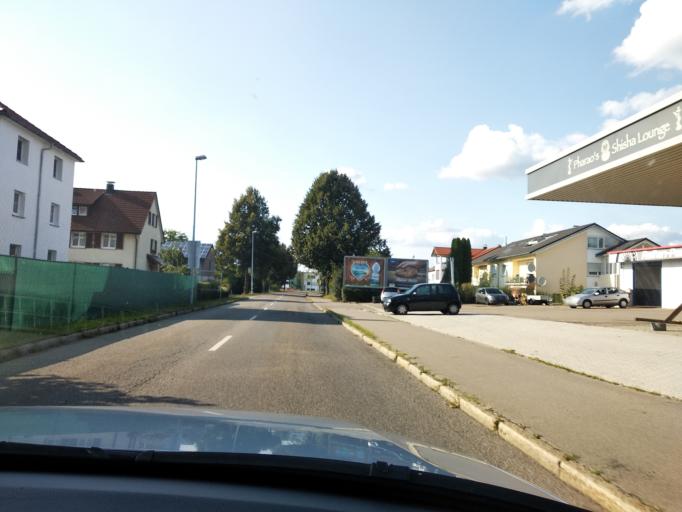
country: DE
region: Baden-Wuerttemberg
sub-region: Tuebingen Region
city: Leutkirch im Allgau
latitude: 47.8352
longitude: 10.0182
